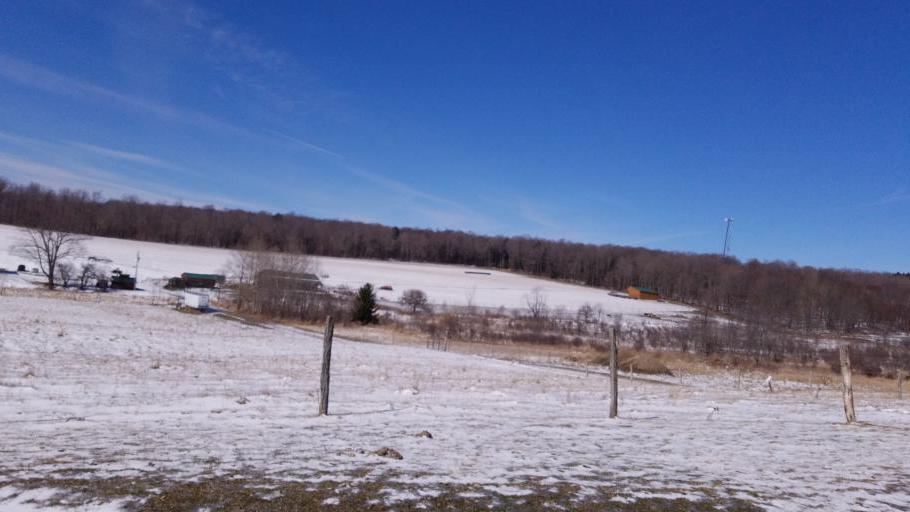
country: US
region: New York
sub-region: Allegany County
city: Andover
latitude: 41.9346
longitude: -77.7749
